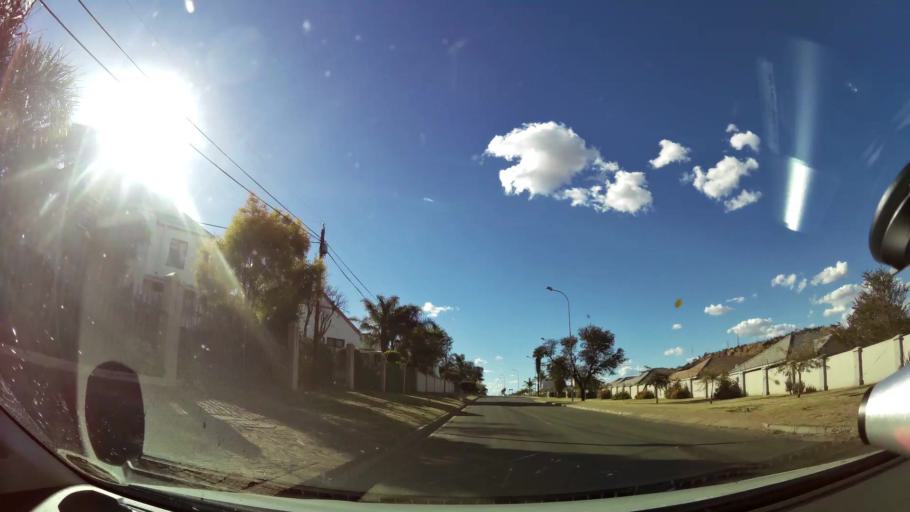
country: ZA
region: North-West
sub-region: Dr Kenneth Kaunda District Municipality
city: Klerksdorp
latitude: -26.8228
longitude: 26.6786
